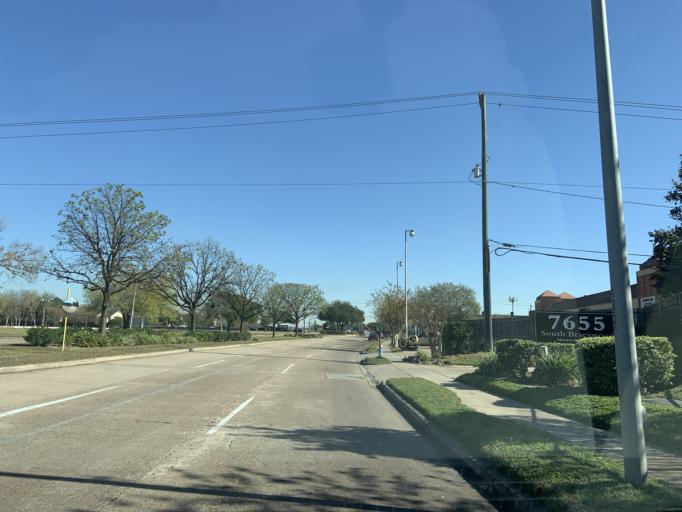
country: US
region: Texas
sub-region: Harris County
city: Bellaire
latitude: 29.6754
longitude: -95.5107
